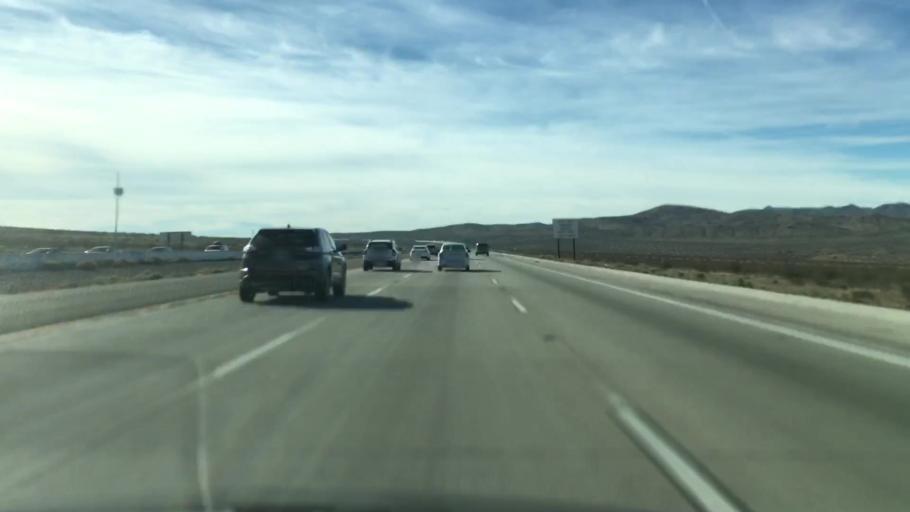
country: US
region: California
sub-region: San Bernardino County
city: Lenwood
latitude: 34.7130
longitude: -117.1995
